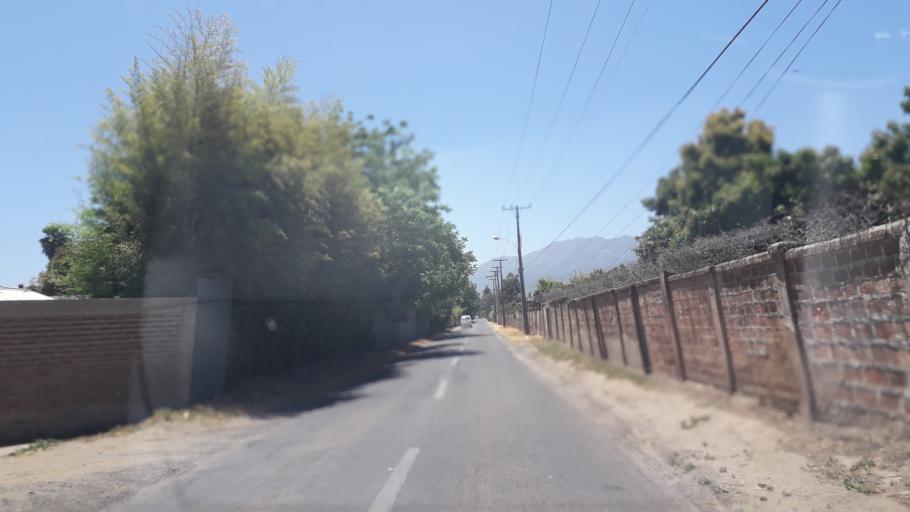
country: CL
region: Valparaiso
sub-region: Provincia de Quillota
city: Quillota
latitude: -32.9209
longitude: -71.2408
